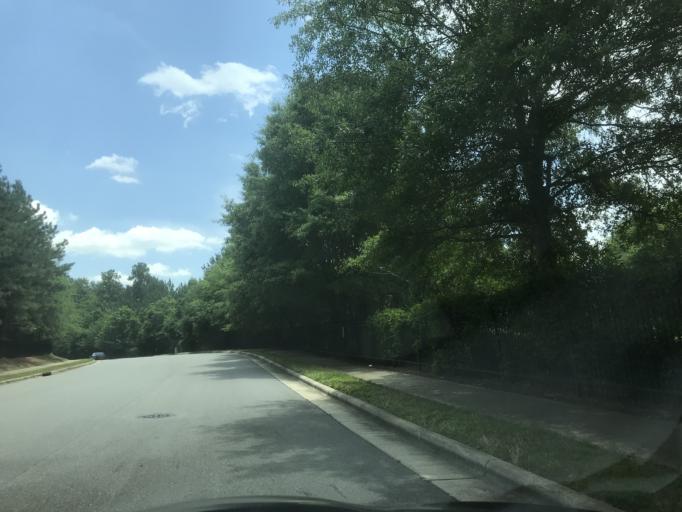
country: US
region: North Carolina
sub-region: Wake County
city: Wake Forest
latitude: 35.9440
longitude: -78.5483
